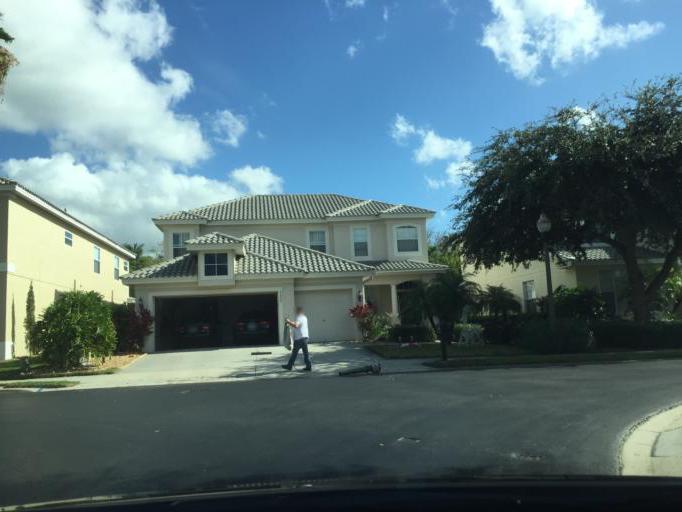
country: US
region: Florida
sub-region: Pinellas County
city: Saint George
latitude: 28.0445
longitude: -82.7456
